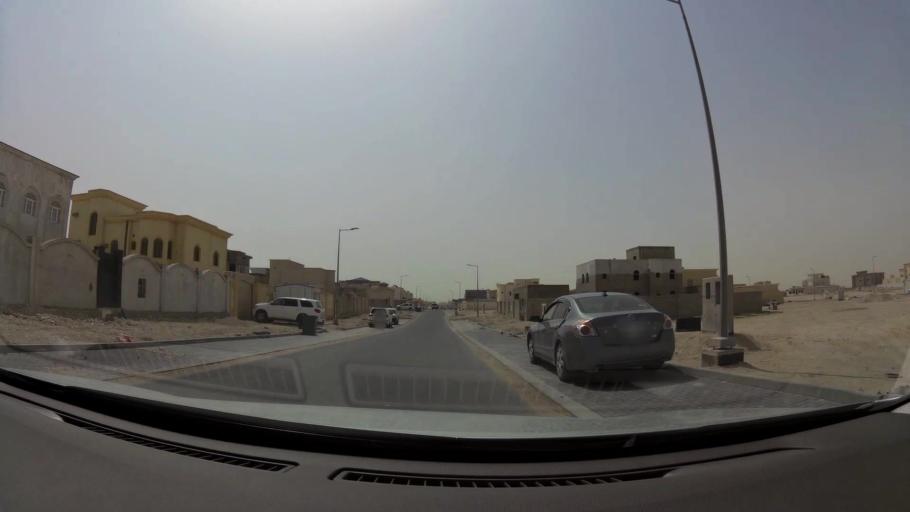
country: QA
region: Baladiyat ar Rayyan
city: Ar Rayyan
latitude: 25.2611
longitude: 51.3738
